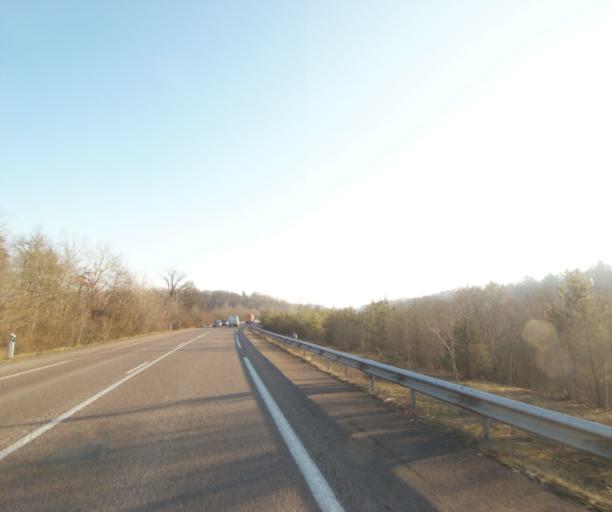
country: FR
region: Champagne-Ardenne
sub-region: Departement de la Haute-Marne
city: Chevillon
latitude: 48.4990
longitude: 5.1081
